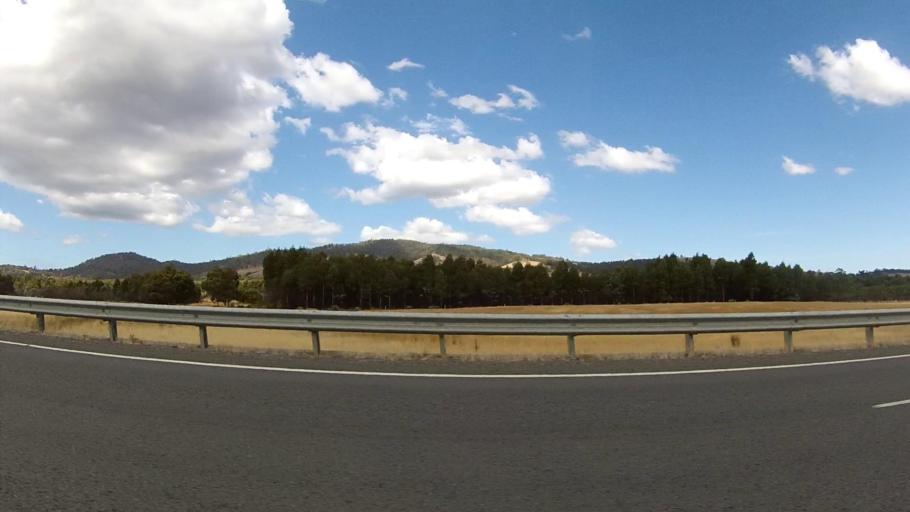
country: AU
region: Tasmania
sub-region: Sorell
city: Sorell
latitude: -42.6430
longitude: 147.5756
